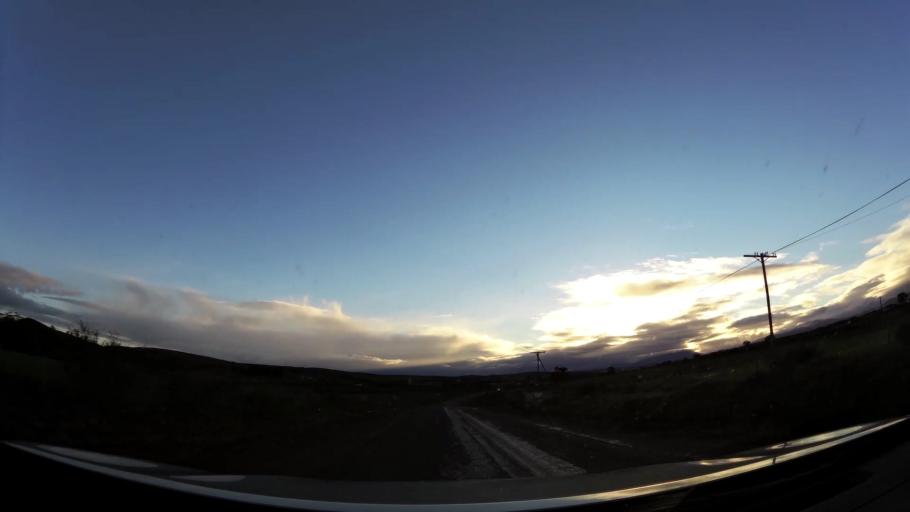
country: ZA
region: Western Cape
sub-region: Eden District Municipality
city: Riversdale
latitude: -34.0817
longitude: 20.9366
